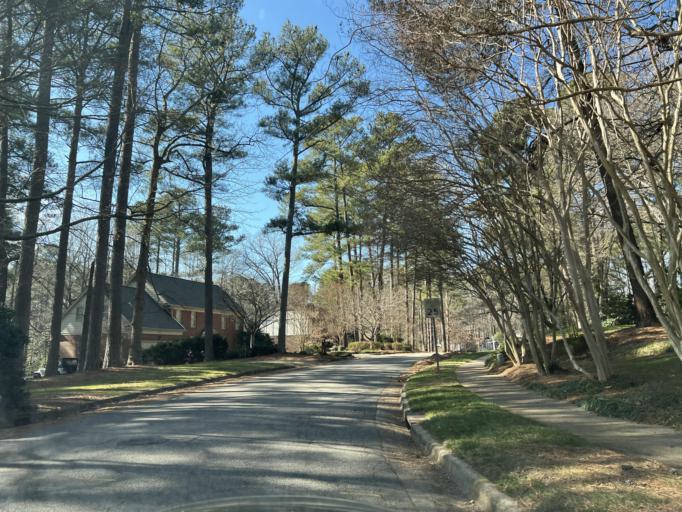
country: US
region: North Carolina
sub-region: Wake County
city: West Raleigh
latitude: 35.8850
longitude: -78.6188
